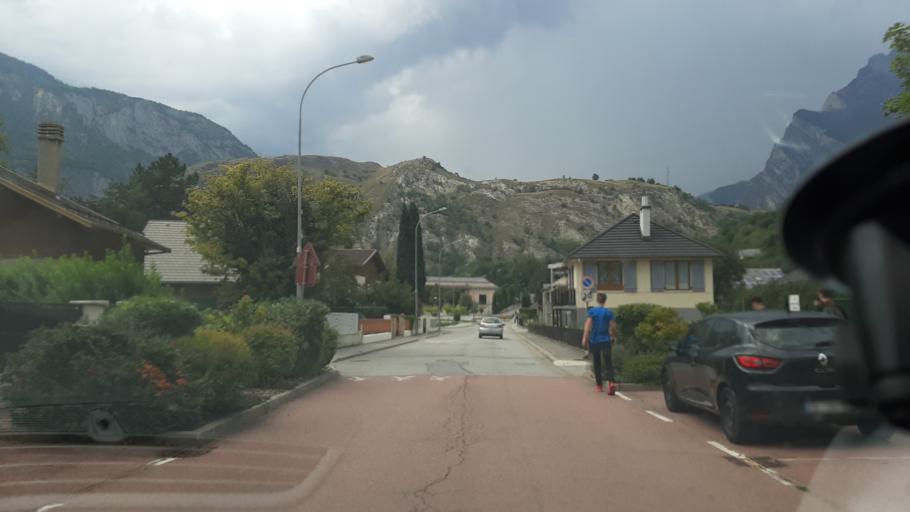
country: FR
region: Rhone-Alpes
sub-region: Departement de la Savoie
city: Saint-Michel-de-Maurienne
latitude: 45.2206
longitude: 6.4675
